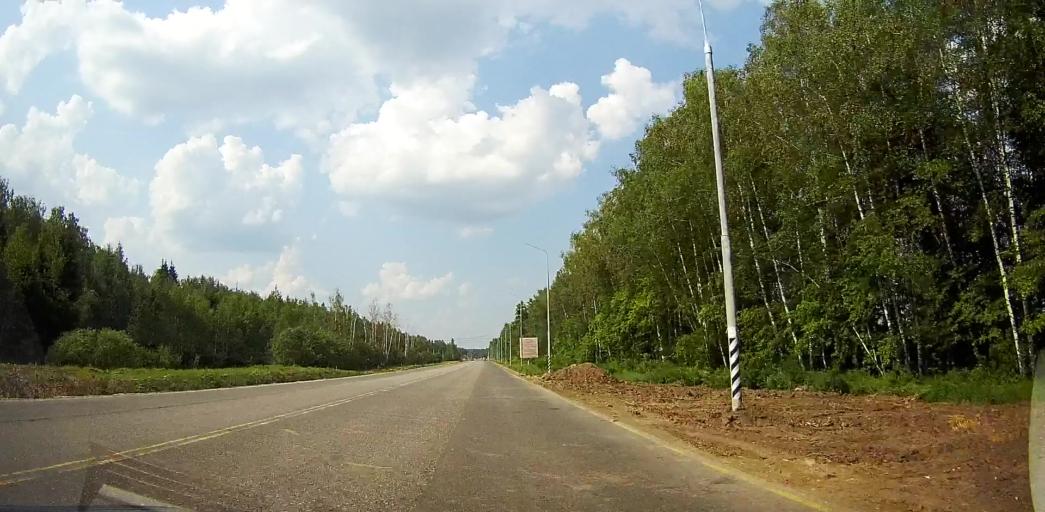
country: RU
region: Moskovskaya
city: Mikhnevo
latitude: 55.0637
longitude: 37.9538
